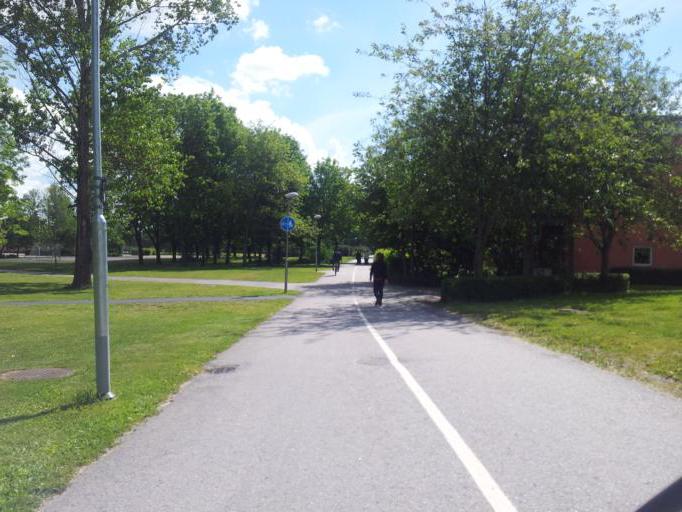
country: SE
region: Uppsala
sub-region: Uppsala Kommun
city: Uppsala
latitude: 59.8753
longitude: 17.6598
